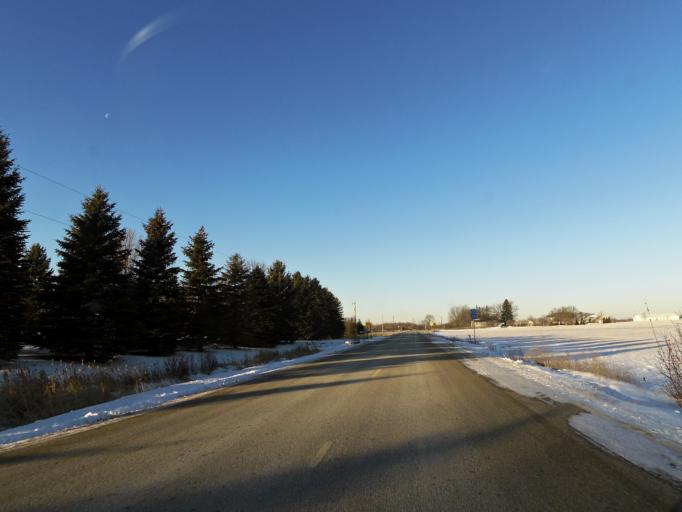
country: US
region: Minnesota
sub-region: Scott County
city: Prior Lake
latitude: 44.6524
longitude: -93.5117
